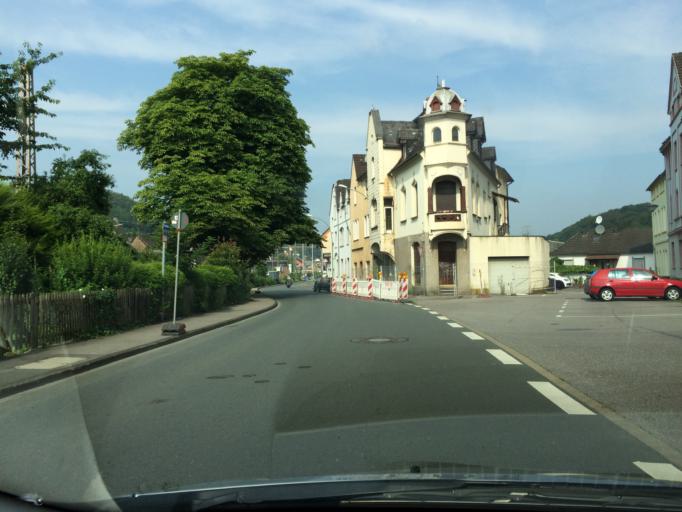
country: DE
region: North Rhine-Westphalia
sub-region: Regierungsbezirk Arnsberg
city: Nachrodt-Wiblingwerde
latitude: 51.3474
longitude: 7.5835
